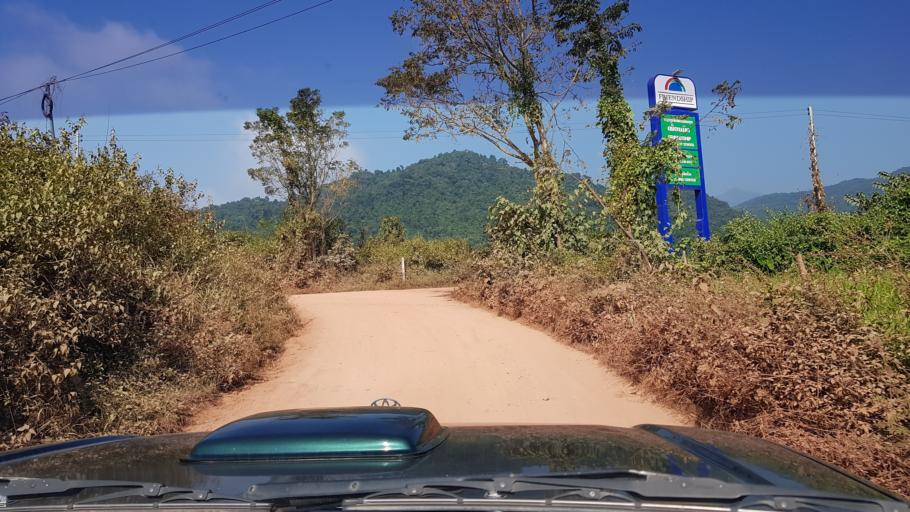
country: LA
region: Oudomxai
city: Muang Xay
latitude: 20.7161
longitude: 102.0406
